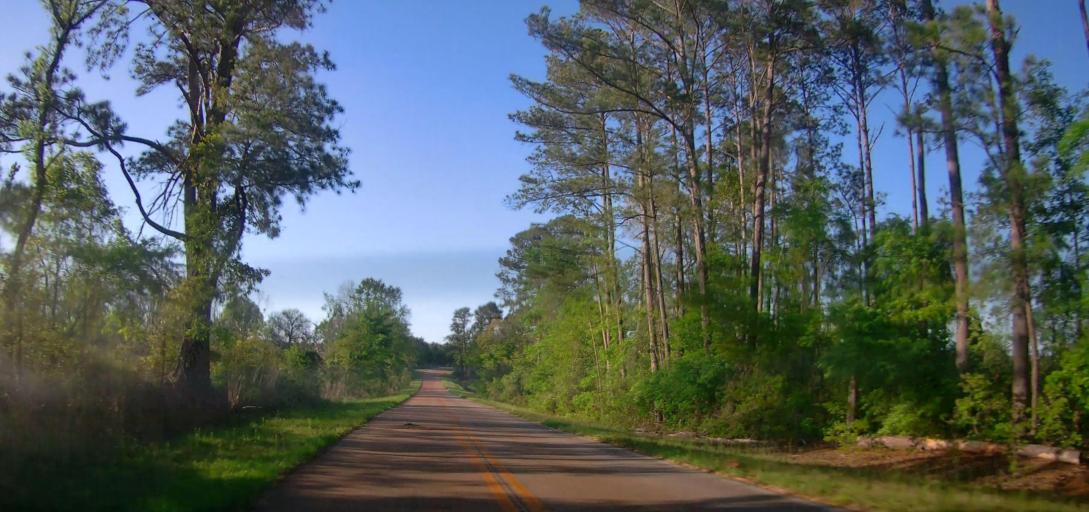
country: US
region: Georgia
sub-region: Macon County
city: Oglethorpe
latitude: 32.2881
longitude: -84.1467
